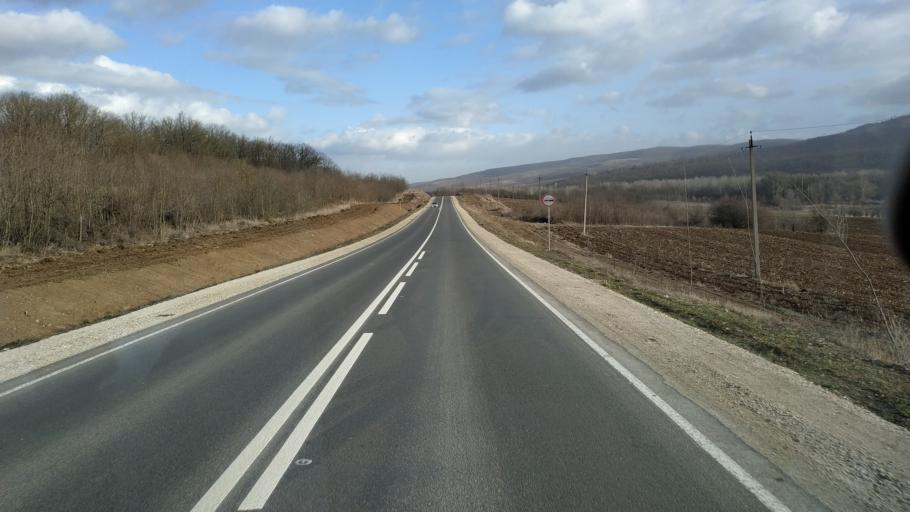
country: MD
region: Calarasi
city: Calarasi
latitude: 47.3098
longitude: 28.1255
